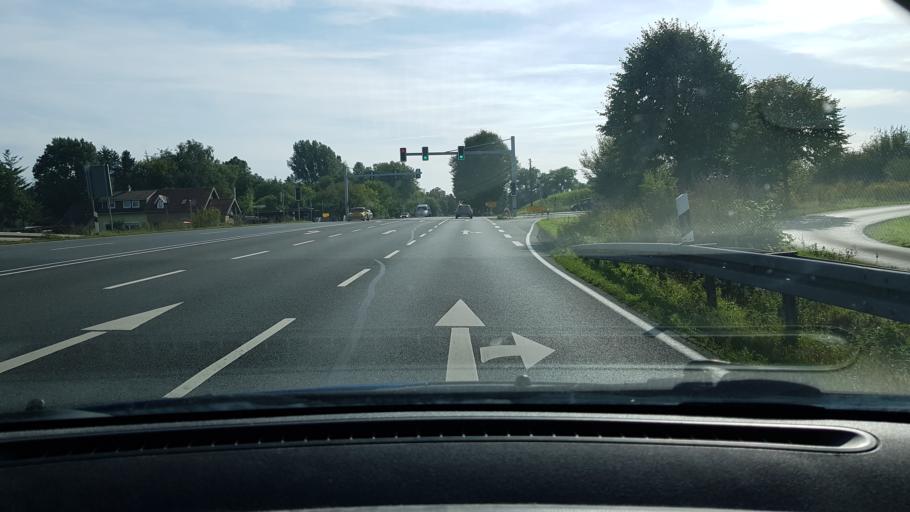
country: DE
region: Lower Saxony
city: Bad Munder am Deister
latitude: 52.1496
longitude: 9.4512
